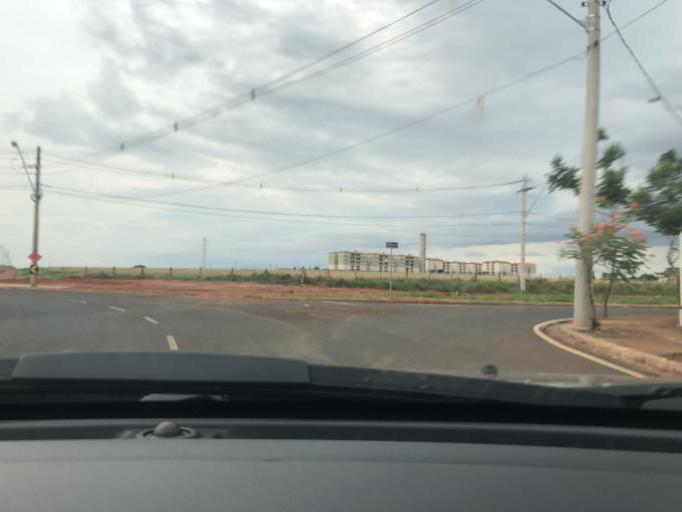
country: BR
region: Sao Paulo
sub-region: Sao Jose Do Rio Preto
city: Sao Jose do Rio Preto
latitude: -20.8381
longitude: -49.4203
